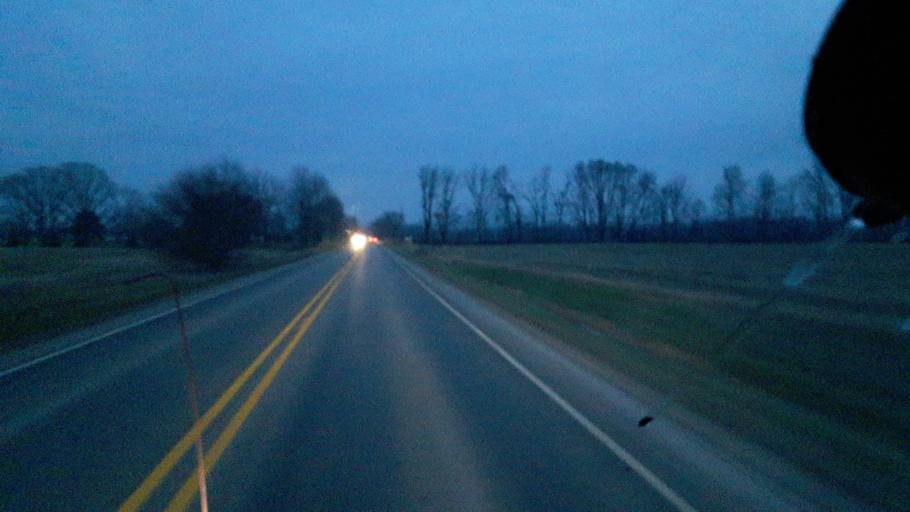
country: US
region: Indiana
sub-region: LaGrange County
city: Lagrange
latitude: 41.6119
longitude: -85.4029
